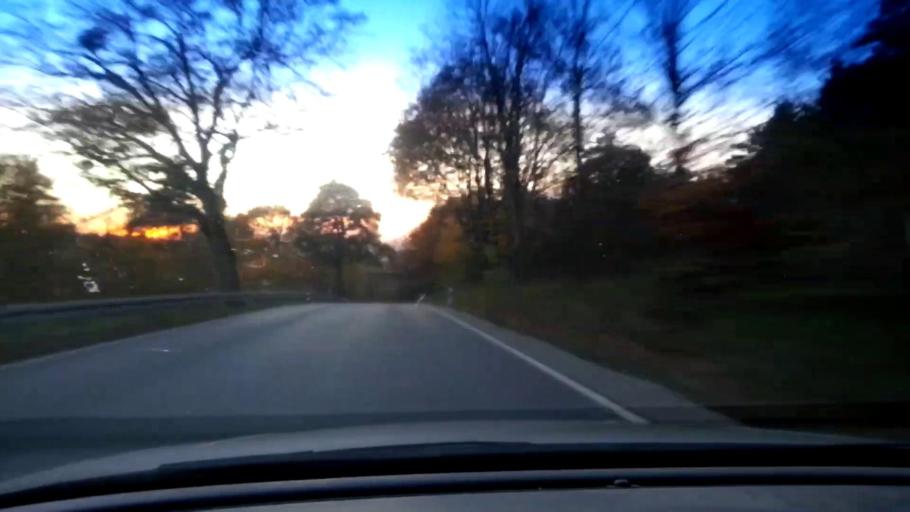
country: DE
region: Bavaria
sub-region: Upper Franconia
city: Poxdorf
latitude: 49.8693
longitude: 11.0818
